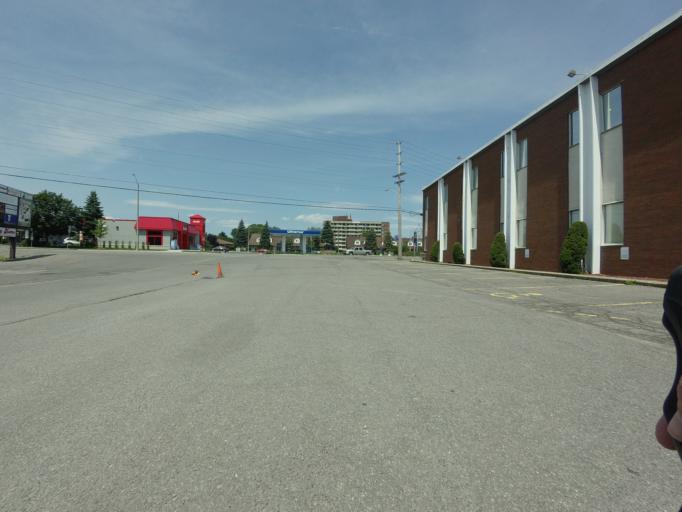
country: CA
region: Ontario
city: Ottawa
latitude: 45.3796
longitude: -75.6395
